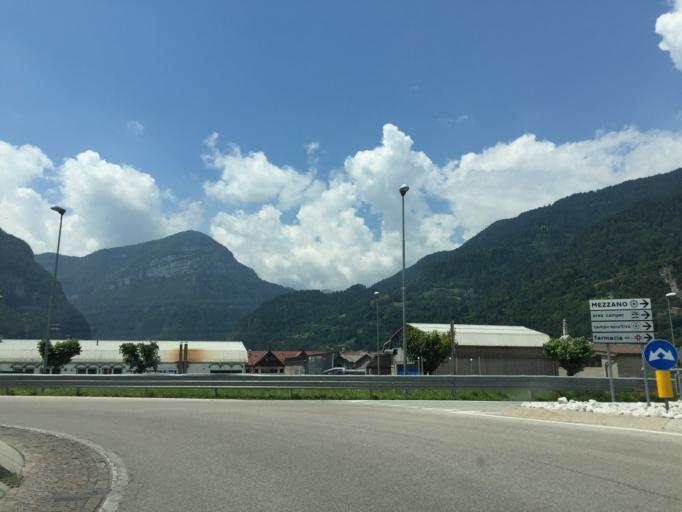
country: IT
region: Trentino-Alto Adige
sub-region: Provincia di Trento
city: Mezzano
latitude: 46.1499
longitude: 11.8075
